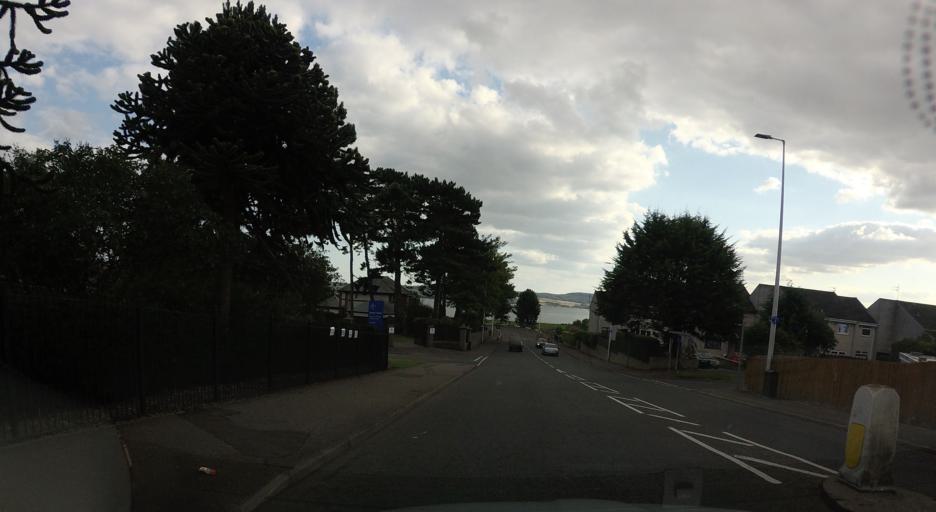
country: GB
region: Scotland
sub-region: Dundee City
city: Dundee
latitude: 56.4559
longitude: -3.0258
